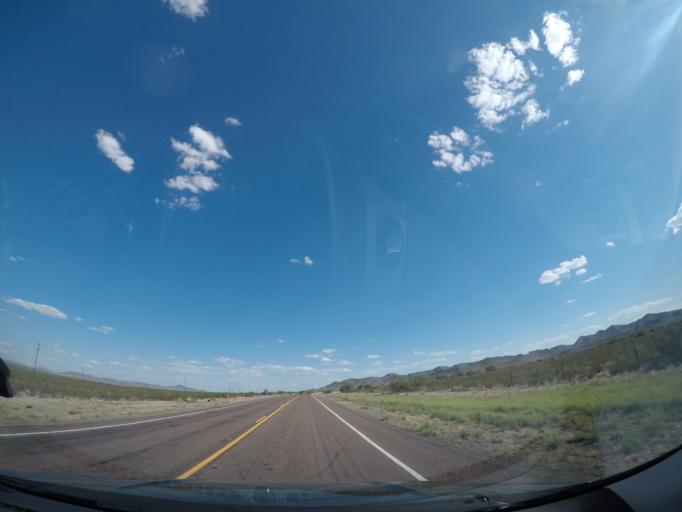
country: US
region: Texas
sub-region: Culberson County
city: Van Horn
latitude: 30.9342
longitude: -104.8098
